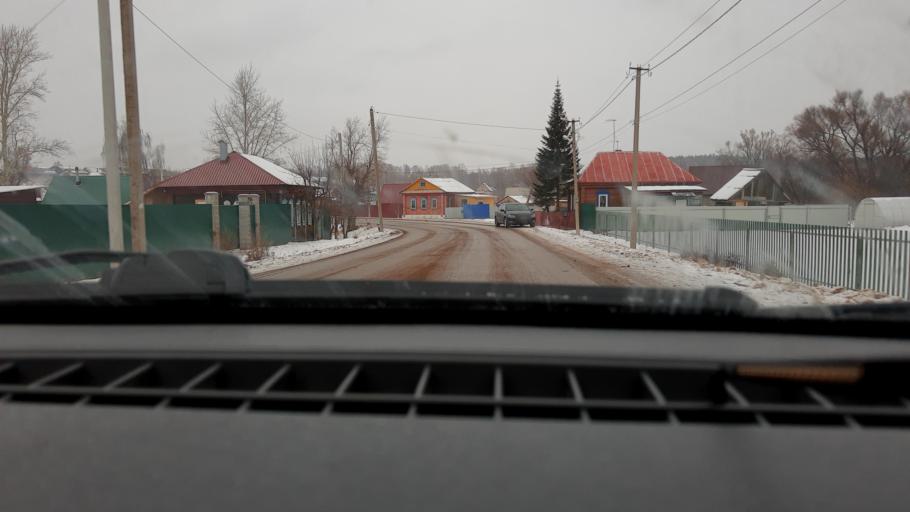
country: RU
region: Bashkortostan
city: Kabakovo
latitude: 54.7039
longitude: 56.2468
